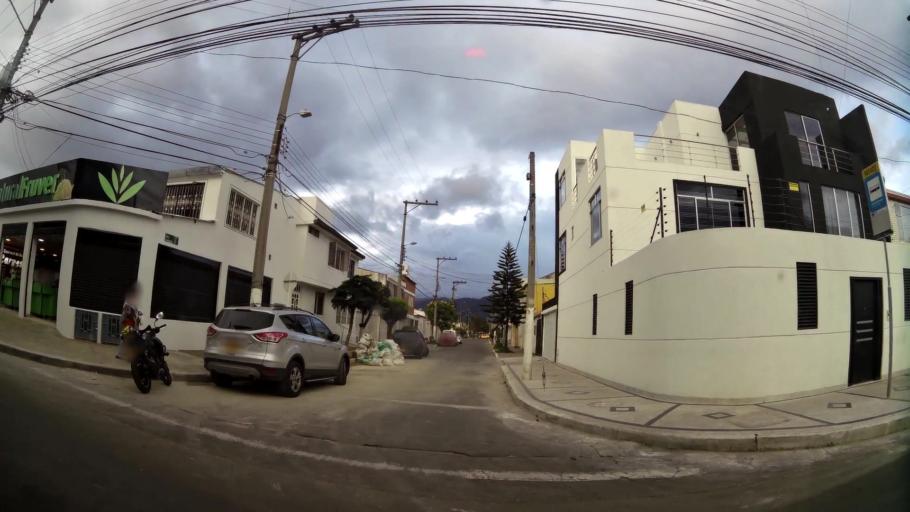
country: CO
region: Bogota D.C.
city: Bogota
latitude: 4.5959
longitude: -74.1209
